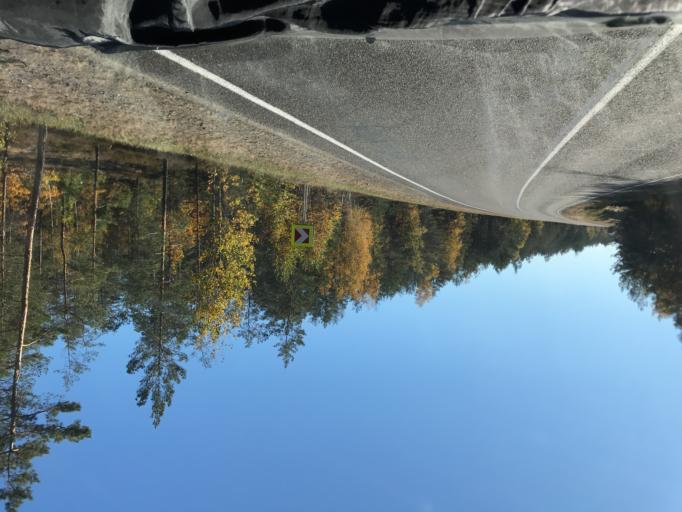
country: BY
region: Gomel
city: Sasnovy Bor
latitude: 52.5325
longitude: 29.3297
